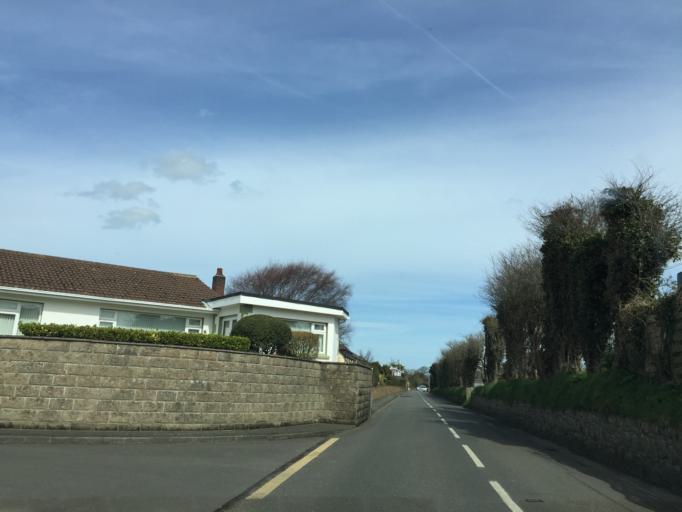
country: JE
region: St Helier
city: Saint Helier
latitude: 49.2322
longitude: -2.1982
